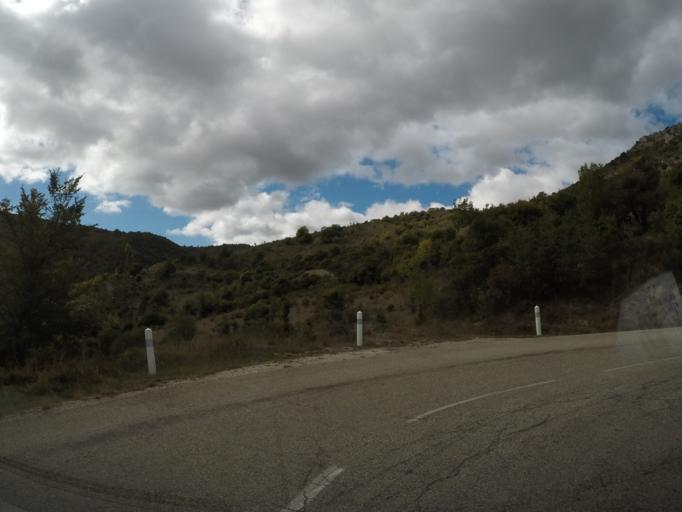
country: FR
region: Provence-Alpes-Cote d'Azur
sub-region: Departement du Vaucluse
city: Sault
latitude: 44.1860
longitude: 5.5337
